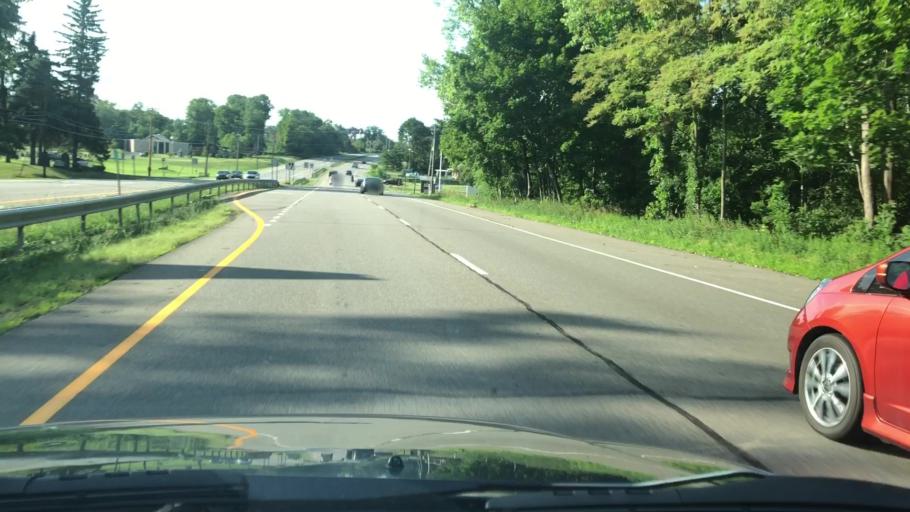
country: US
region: New York
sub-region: Dutchess County
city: Fishkill
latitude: 41.5410
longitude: -73.9017
